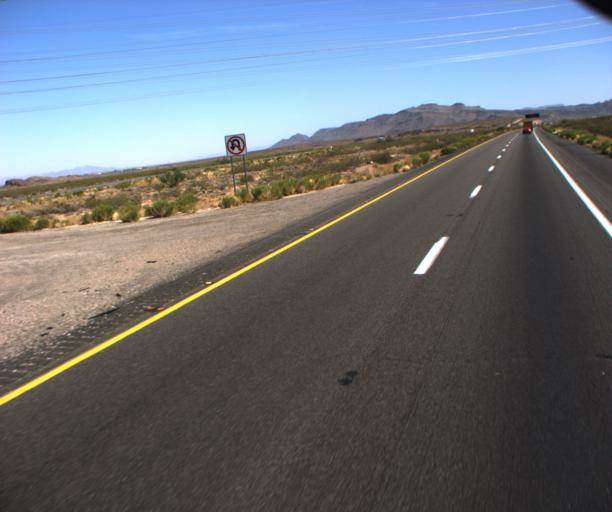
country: US
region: Arizona
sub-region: Mohave County
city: Kingman
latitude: 35.1043
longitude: -114.1168
